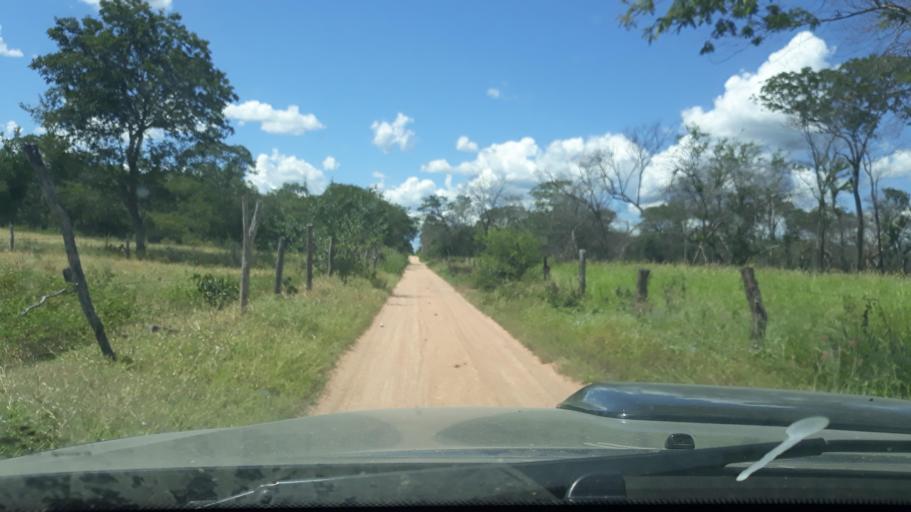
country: BR
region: Bahia
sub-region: Riacho De Santana
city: Riacho de Santana
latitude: -13.8671
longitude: -43.0182
